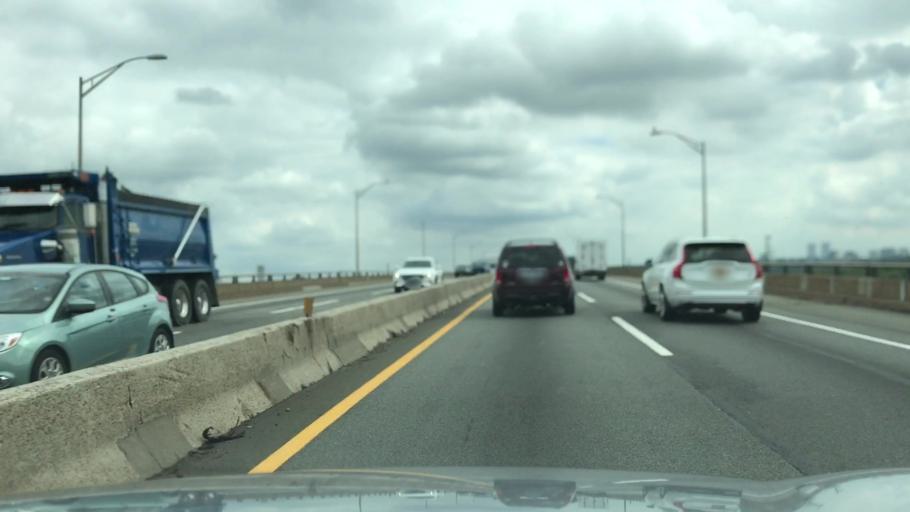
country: US
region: New Jersey
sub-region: Bergen County
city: Moonachie
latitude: 40.8217
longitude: -74.0356
